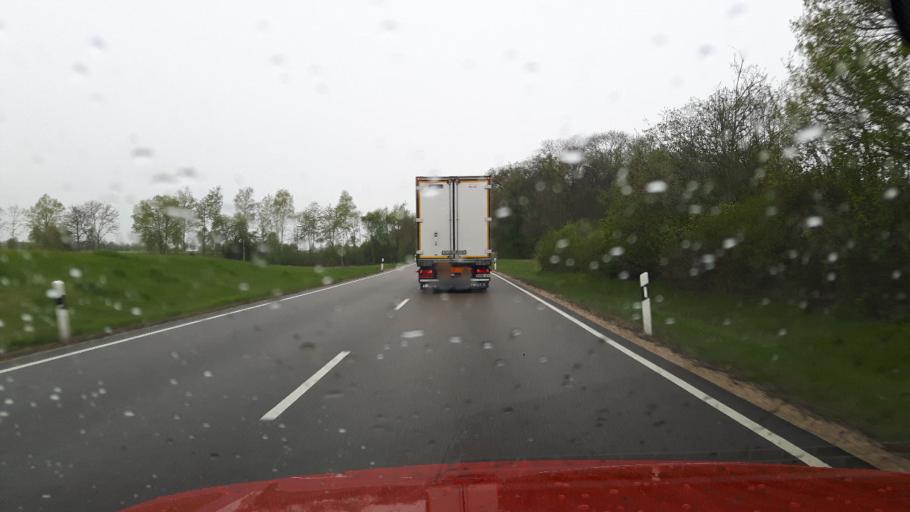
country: DE
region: Bavaria
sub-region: Regierungsbezirk Mittelfranken
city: Weidenbach
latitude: 49.2099
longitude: 10.6566
